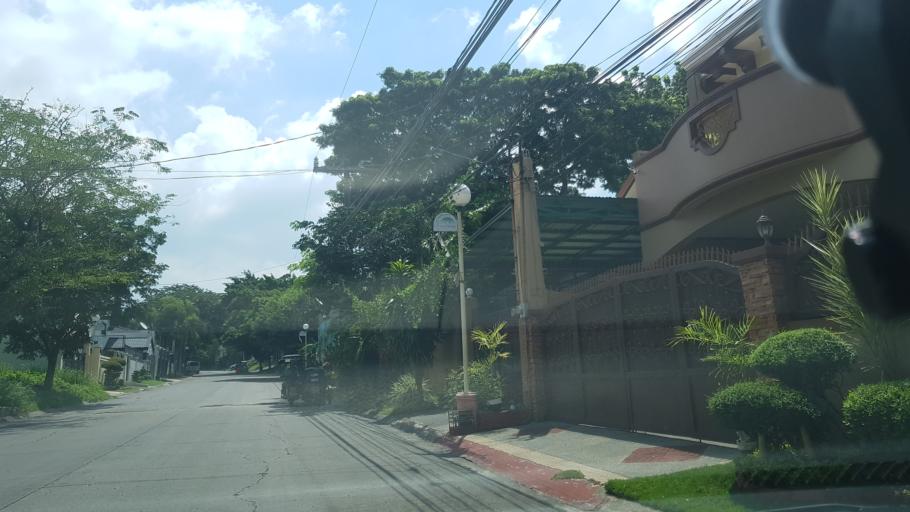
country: PH
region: Calabarzon
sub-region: Province of Rizal
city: Las Pinas
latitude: 14.4269
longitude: 120.9891
